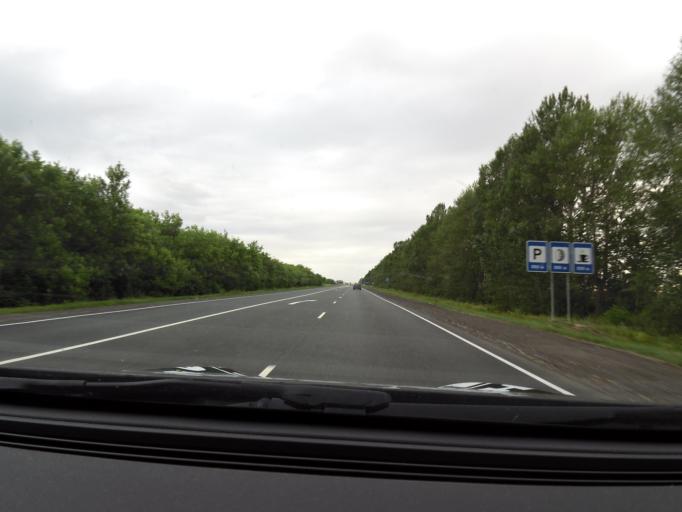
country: RU
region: Chuvashia
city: Yantikovo
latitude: 55.8063
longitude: 47.9389
